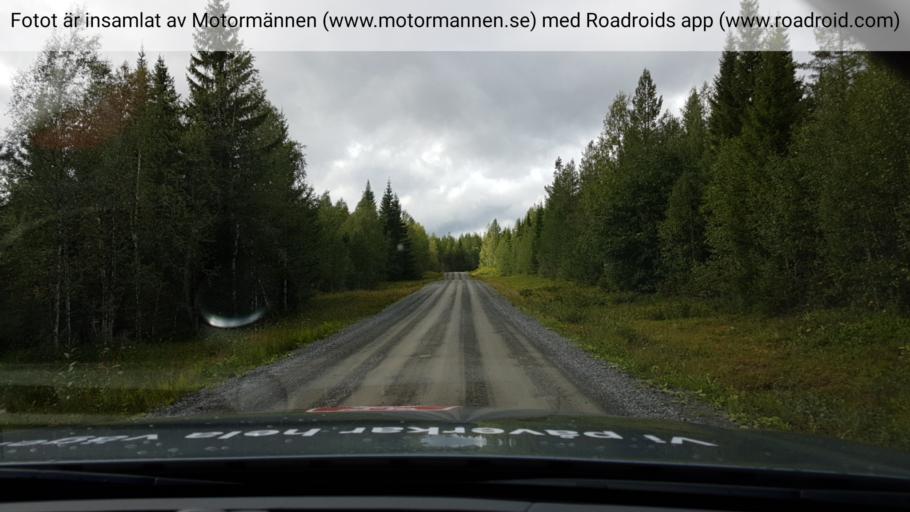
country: SE
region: Jaemtland
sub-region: Krokoms Kommun
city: Krokom
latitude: 63.7402
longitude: 14.4747
